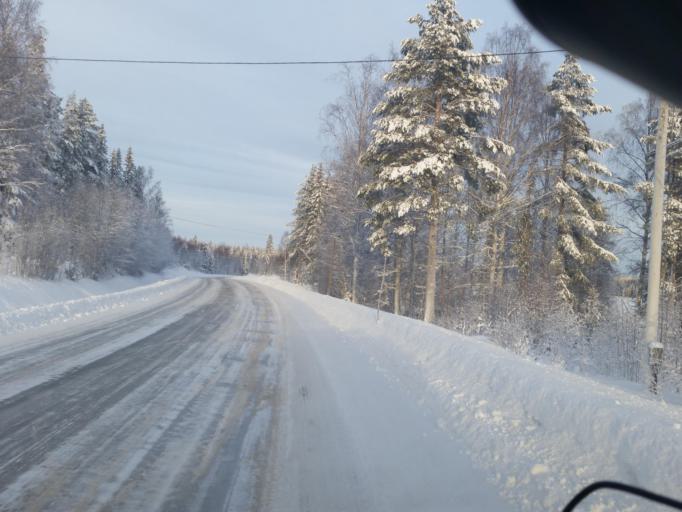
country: SE
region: Norrbotten
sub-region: Pitea Kommun
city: Norrfjarden
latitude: 65.4734
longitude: 21.4722
